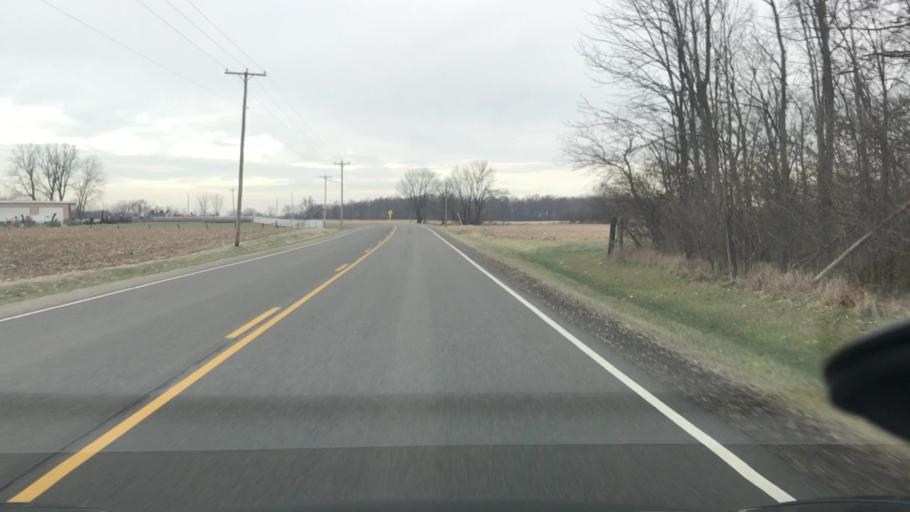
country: US
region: Ohio
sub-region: Madison County
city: London
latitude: 39.8722
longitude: -83.4227
